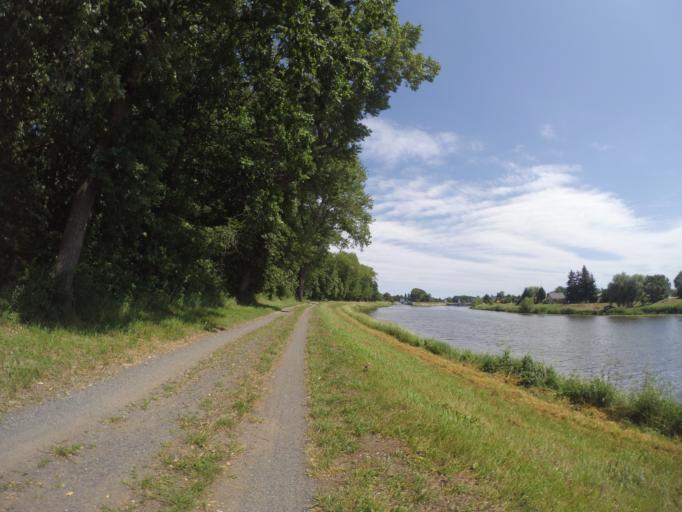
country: CZ
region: Central Bohemia
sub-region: Okres Nymburk
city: Sadska
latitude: 50.1727
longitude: 14.9332
